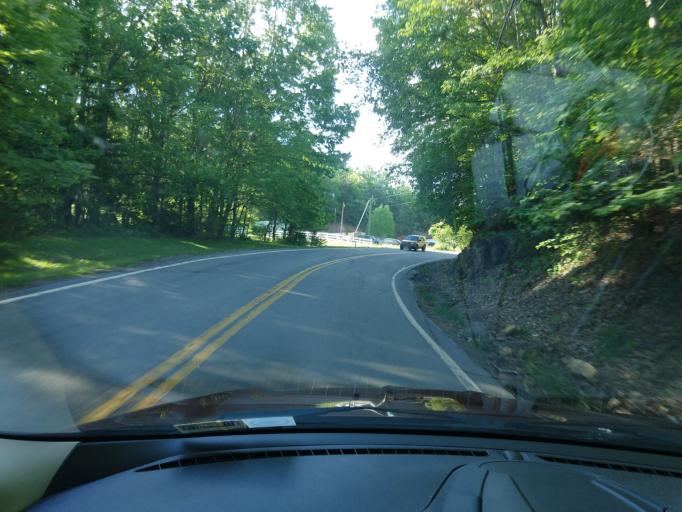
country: US
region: Virginia
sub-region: City of Galax
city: Galax
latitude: 36.7561
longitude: -80.9824
